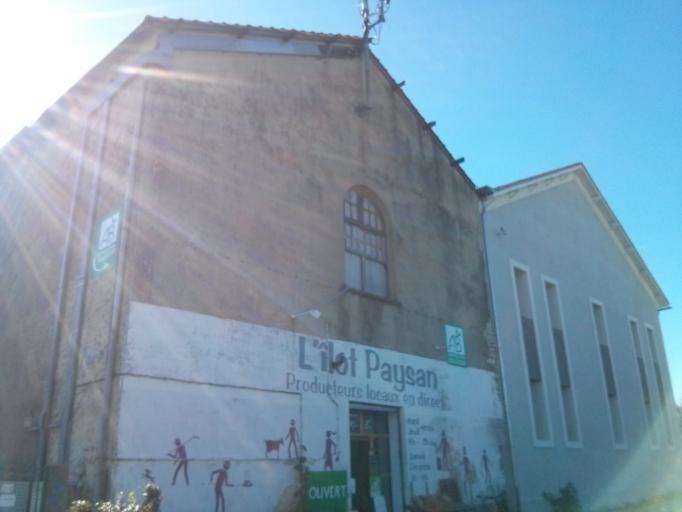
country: FR
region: Languedoc-Roussillon
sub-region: Departement du Gard
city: Congenies
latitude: 43.7735
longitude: 4.1600
